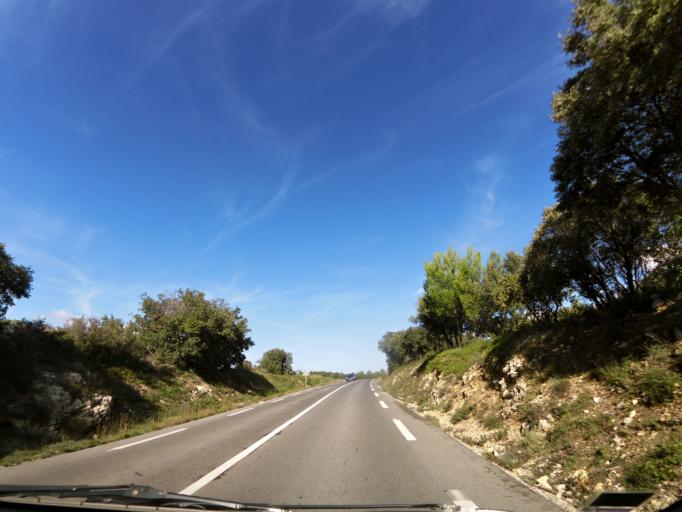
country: FR
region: Languedoc-Roussillon
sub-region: Departement du Gard
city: Villevieille
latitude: 43.8568
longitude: 4.0970
